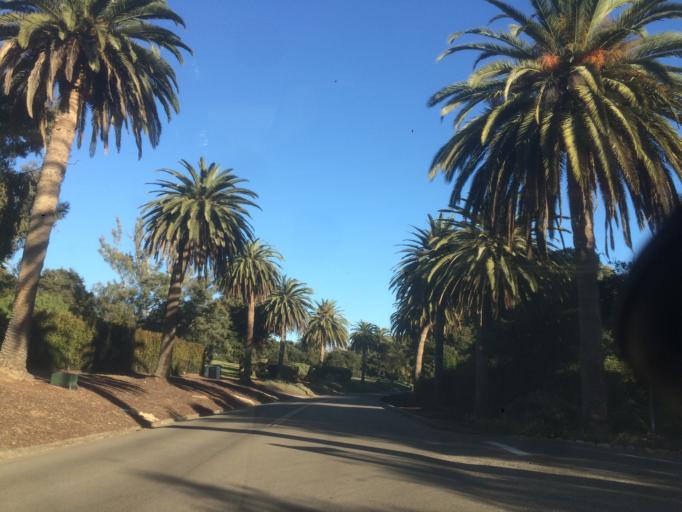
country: US
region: California
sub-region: Santa Barbara County
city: Goleta
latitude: 34.4122
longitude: -119.7664
